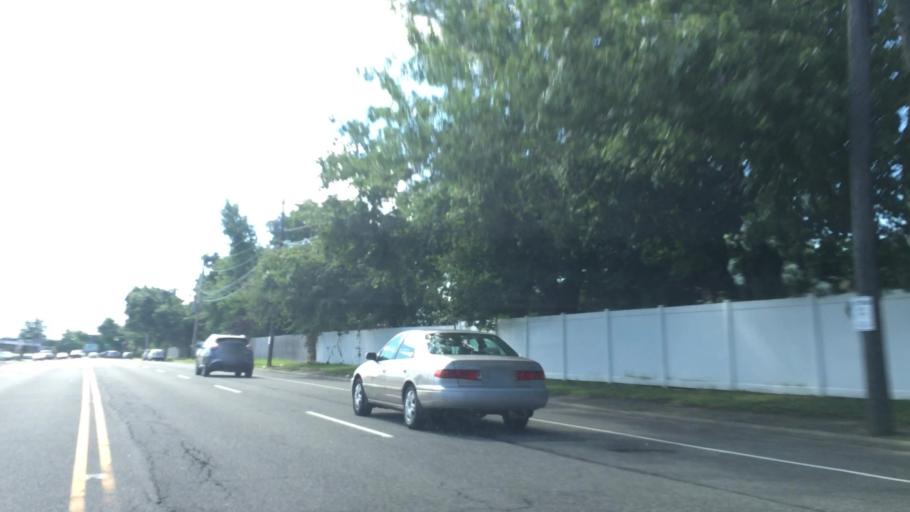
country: US
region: New York
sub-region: Nassau County
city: Jericho
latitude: 40.7997
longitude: -73.5206
